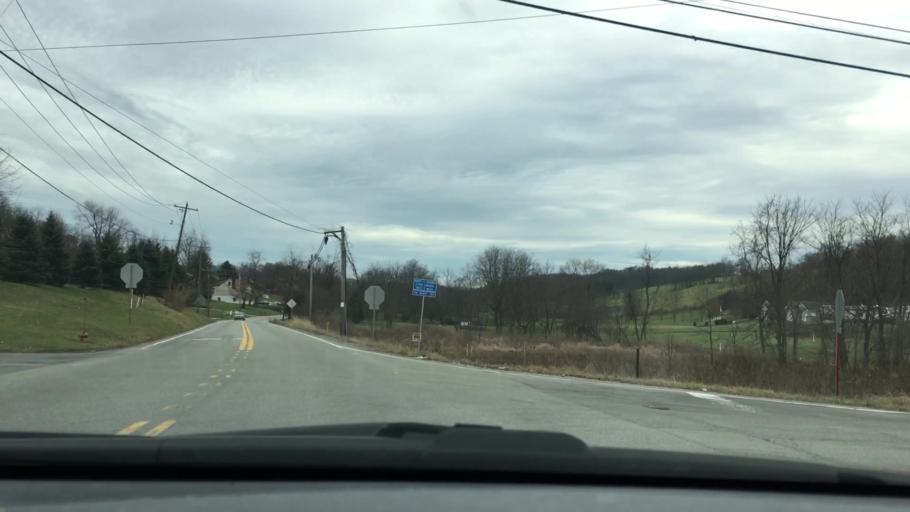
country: US
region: Pennsylvania
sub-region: Washington County
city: Muse
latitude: 40.2837
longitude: -80.2101
